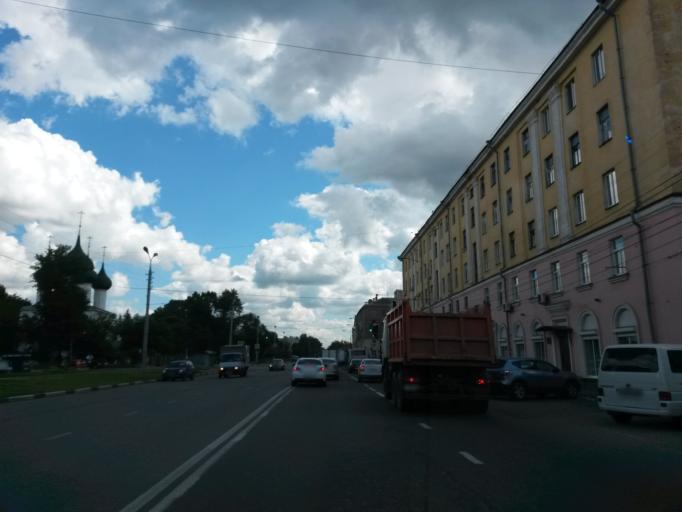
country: RU
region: Jaroslavl
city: Yaroslavl
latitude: 57.6088
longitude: 39.8631
